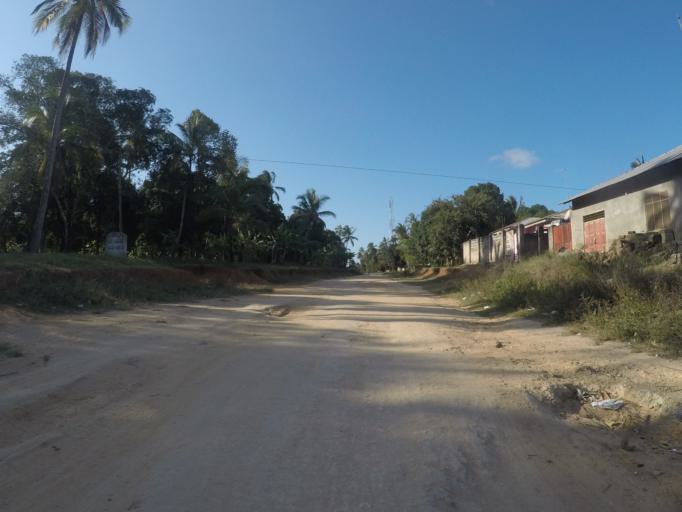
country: TZ
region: Zanzibar Central/South
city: Koani
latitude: -6.1614
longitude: 39.2871
